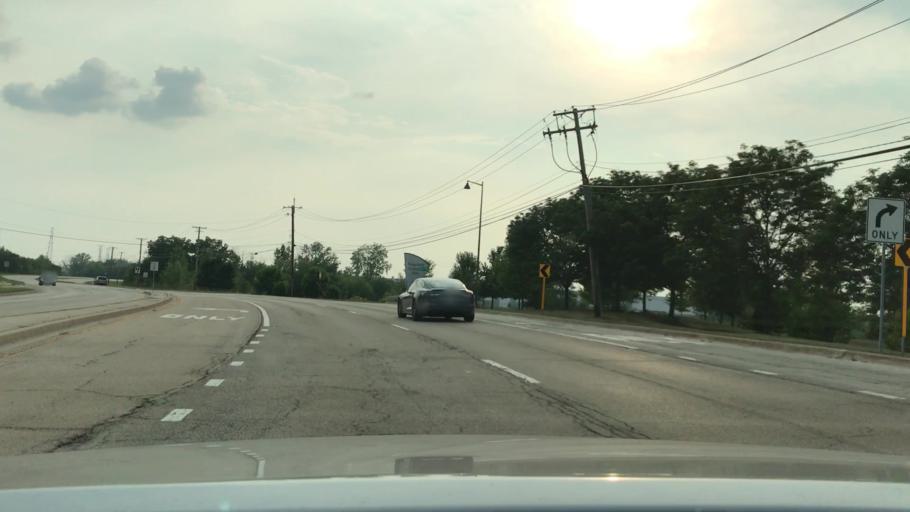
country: US
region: Illinois
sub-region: DuPage County
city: Warrenville
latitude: 41.8104
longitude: -88.2161
